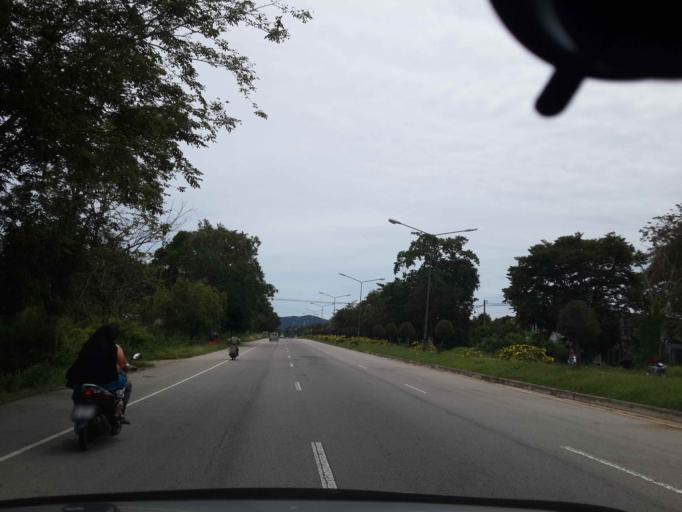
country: TH
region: Narathiwat
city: Narathiwat
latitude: 6.4082
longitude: 101.7902
